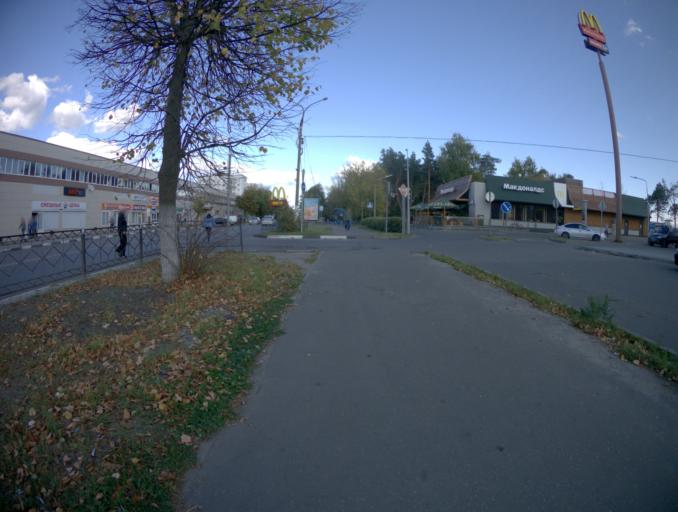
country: RU
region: Moskovskaya
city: Shatura
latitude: 55.5753
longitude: 39.5227
